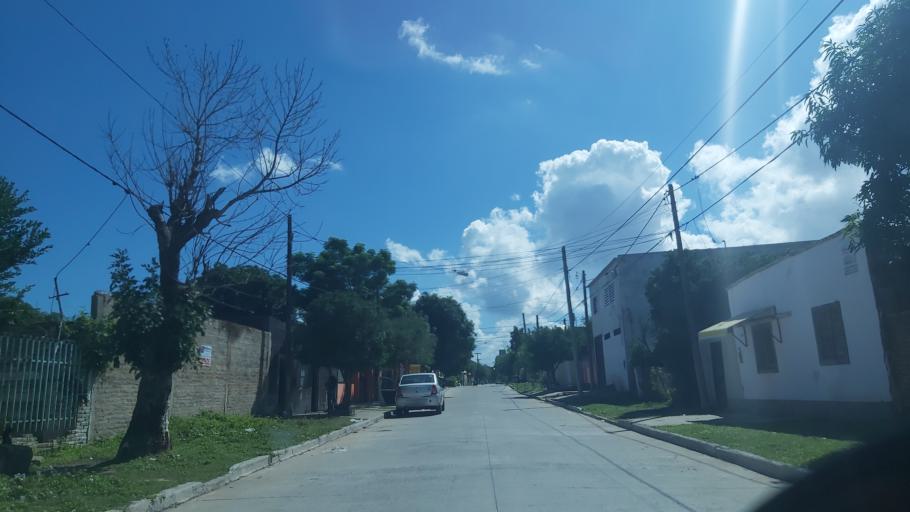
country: AR
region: Corrientes
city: Corrientes
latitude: -27.4809
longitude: -58.8504
